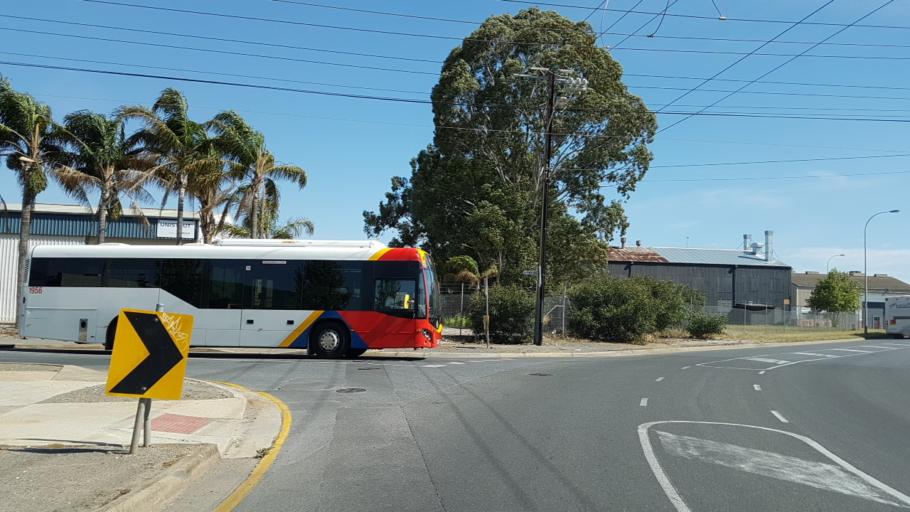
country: AU
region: South Australia
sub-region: Charles Sturt
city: Woodville North
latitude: -34.8597
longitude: 138.5385
